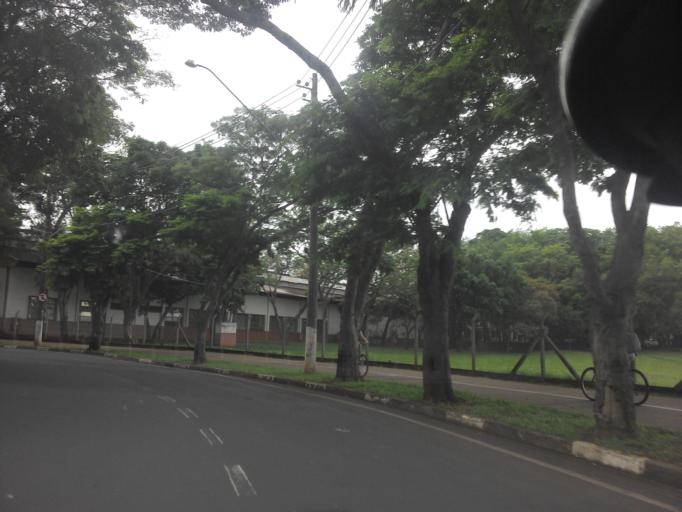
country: BR
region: Sao Paulo
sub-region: Campinas
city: Campinas
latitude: -22.8186
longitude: -47.0723
